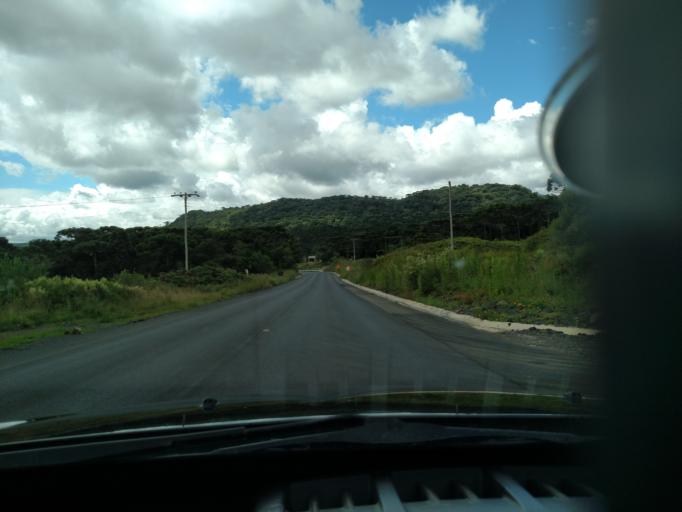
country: BR
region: Santa Catarina
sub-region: Lages
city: Lages
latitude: -27.9417
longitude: -50.0953
